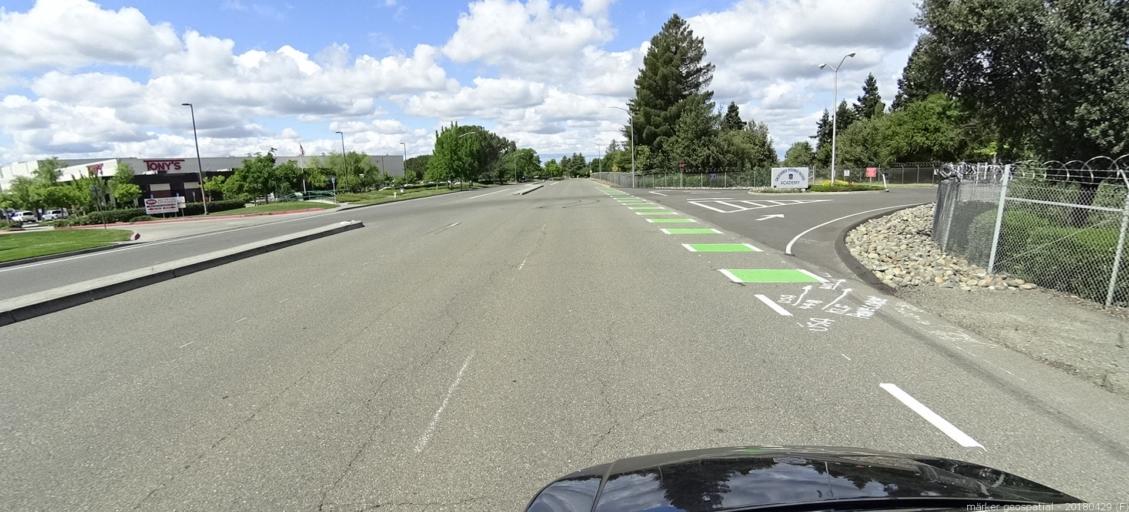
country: US
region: California
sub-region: Yolo County
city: West Sacramento
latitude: 38.5925
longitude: -121.5588
